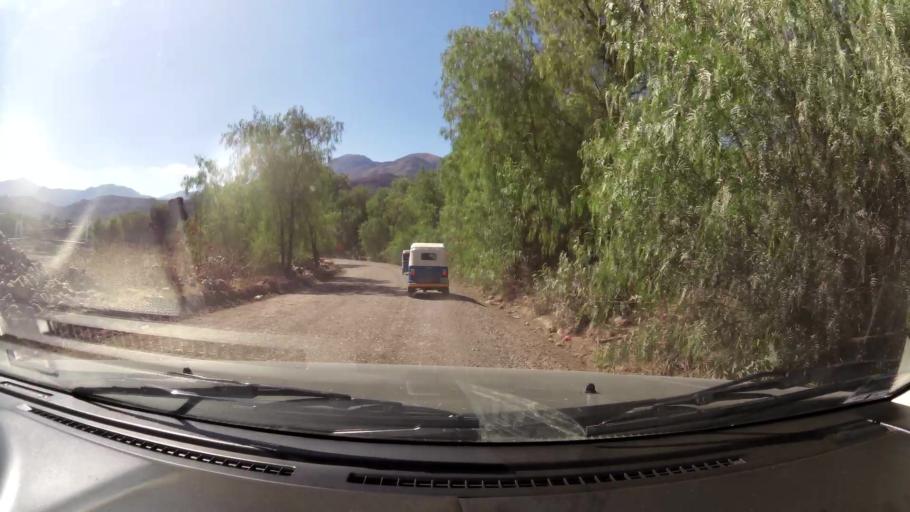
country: PE
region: Ayacucho
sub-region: Provincia de Huanta
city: Luricocha
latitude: -12.8459
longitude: -74.3303
